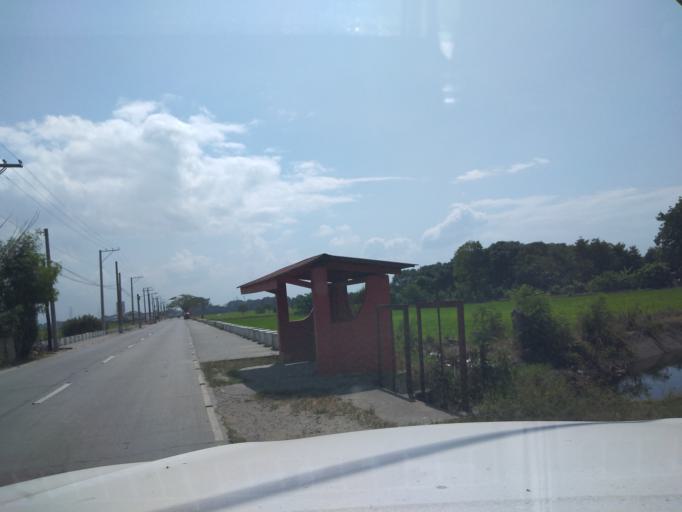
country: PH
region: Central Luzon
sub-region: Province of Pampanga
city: Talang
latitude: 15.0257
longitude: 120.8380
